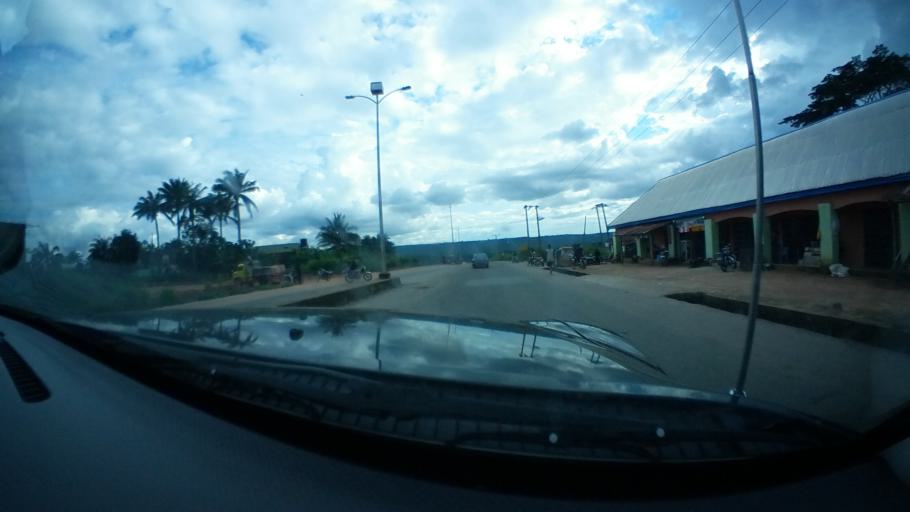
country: NG
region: Imo
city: Orlu
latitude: 5.8257
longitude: 7.0732
